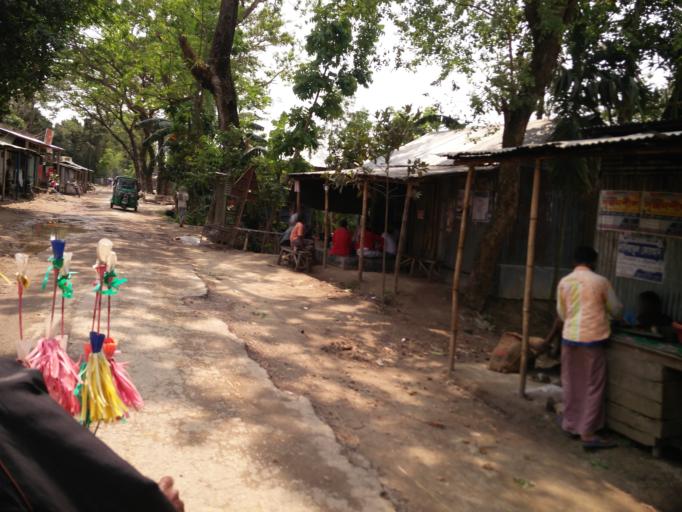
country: BD
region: Dhaka
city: Sherpur
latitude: 24.9447
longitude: 90.1603
